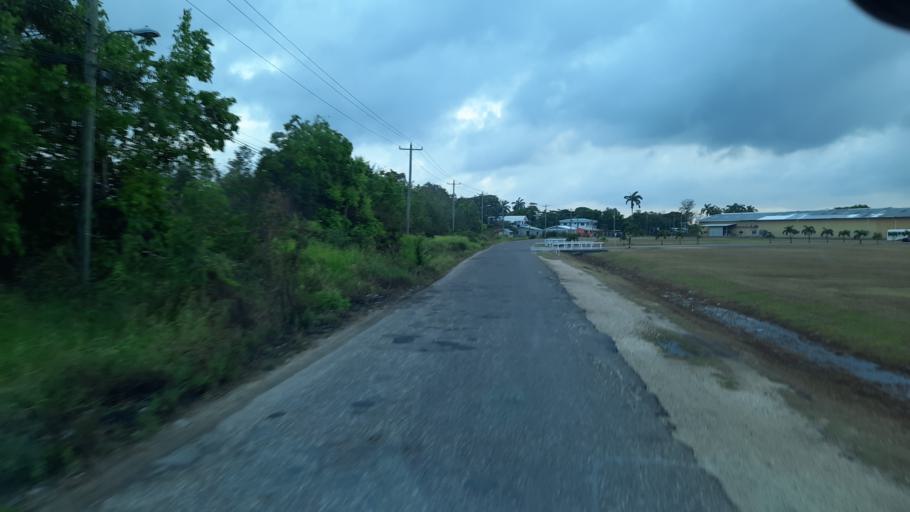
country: BZ
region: Belize
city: Belize City
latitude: 17.5459
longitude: -88.2962
